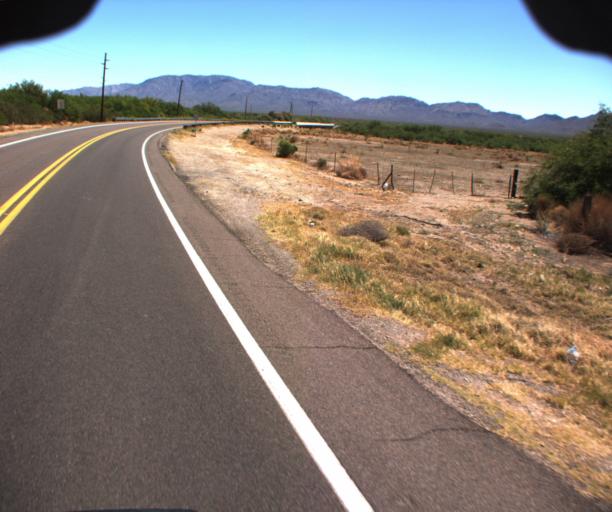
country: US
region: Arizona
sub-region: La Paz County
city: Salome
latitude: 33.8247
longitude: -113.5365
